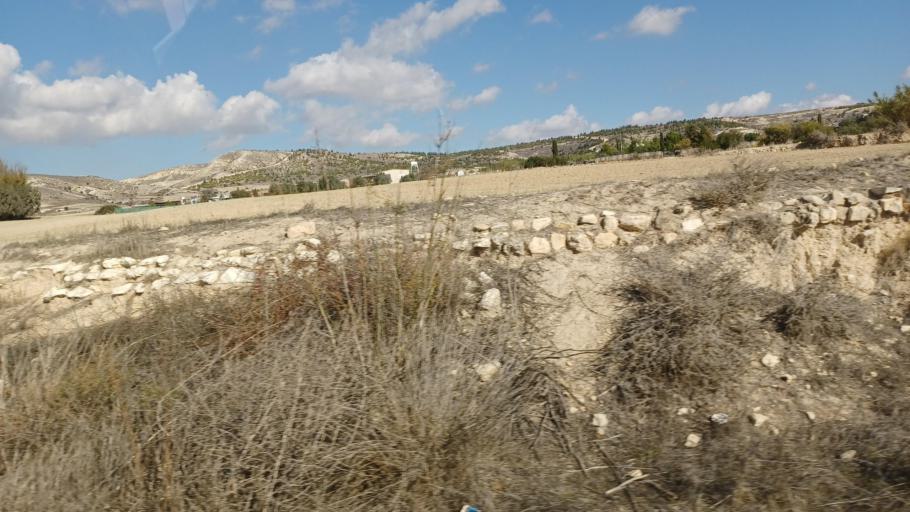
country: CY
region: Larnaka
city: Voroklini
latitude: 35.0050
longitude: 33.6502
